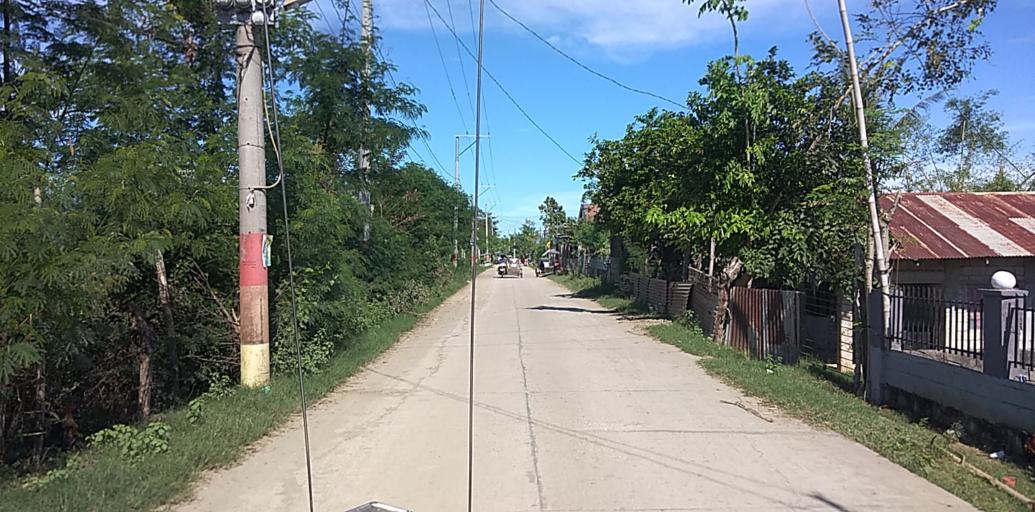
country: PH
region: Central Luzon
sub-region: Province of Pampanga
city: Candaba
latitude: 15.1196
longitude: 120.8136
